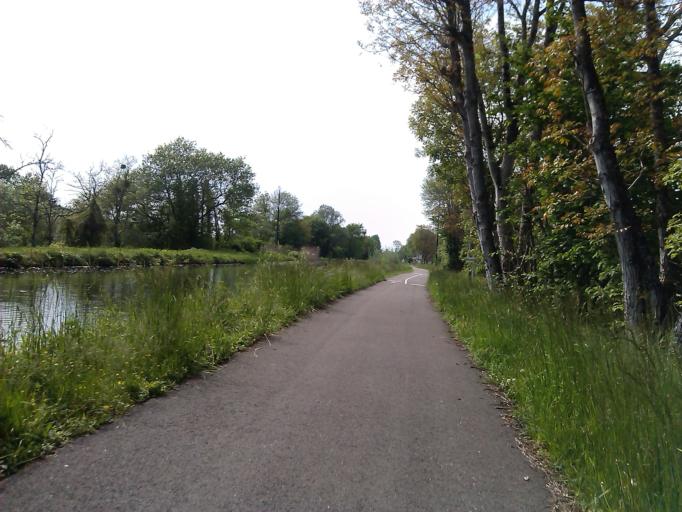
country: FR
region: Franche-Comte
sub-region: Departement du Doubs
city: Saint-Vit
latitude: 47.1660
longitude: 5.8458
